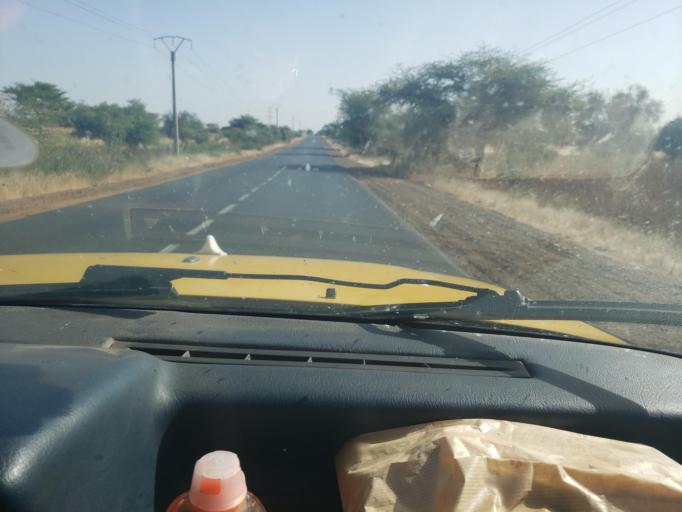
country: SN
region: Louga
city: Louga
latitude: 15.6605
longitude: -16.2577
